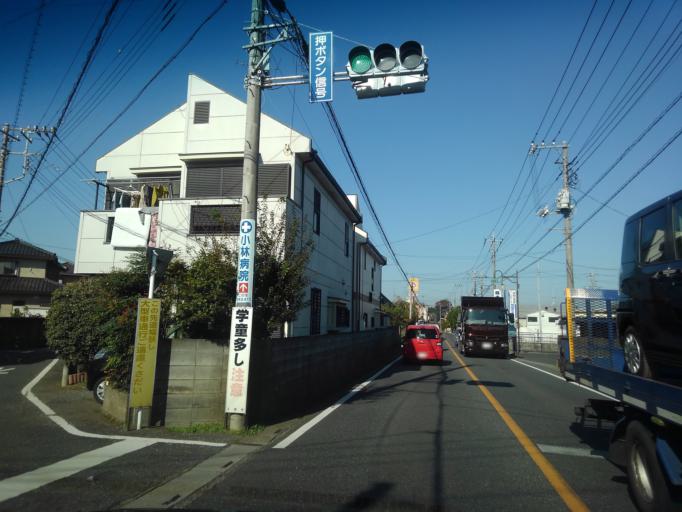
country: JP
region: Saitama
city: Sayama
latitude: 35.7925
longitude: 139.3865
